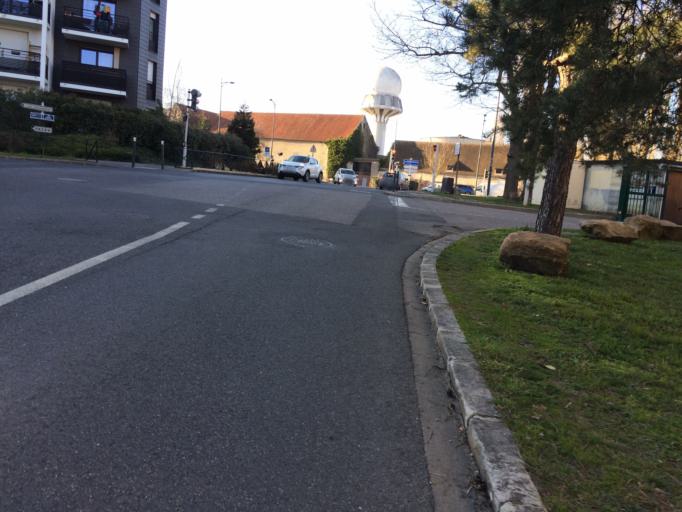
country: FR
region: Ile-de-France
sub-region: Departement de l'Essonne
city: Villebon-sur-Yvette
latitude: 48.7156
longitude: 2.2382
